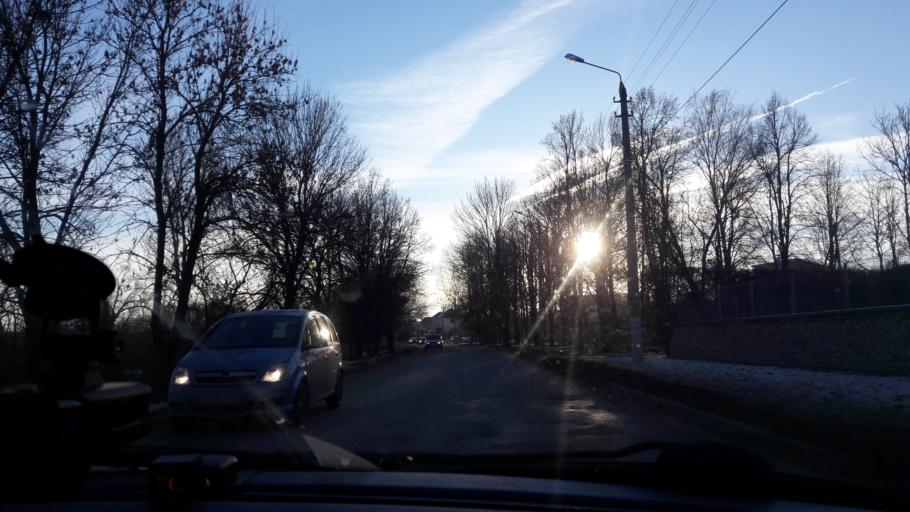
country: RU
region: Tula
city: Gorelki
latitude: 54.2349
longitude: 37.6418
